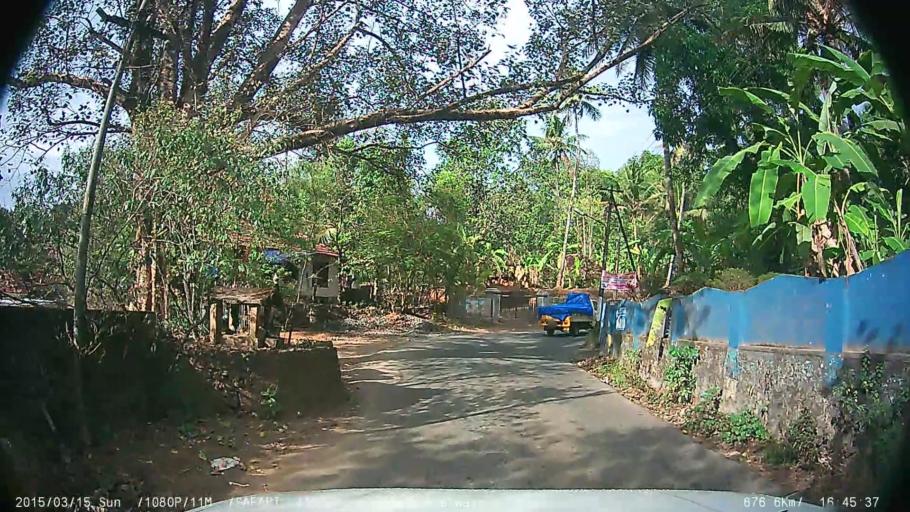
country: IN
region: Kerala
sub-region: Ernakulam
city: Piravam
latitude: 9.8604
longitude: 76.5997
